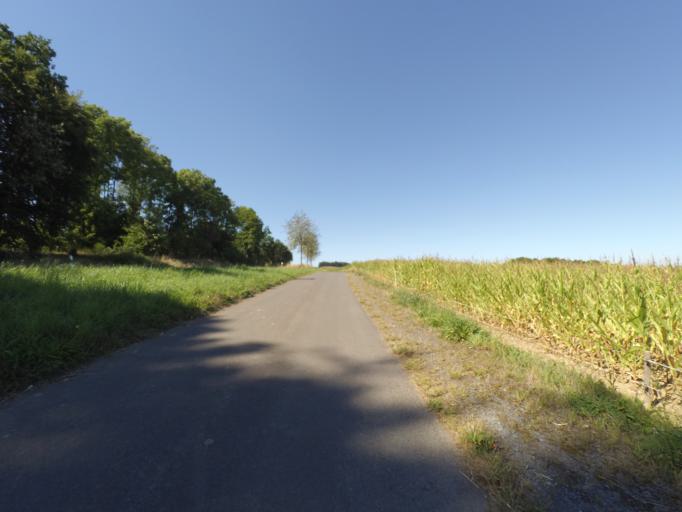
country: DE
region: Rheinland-Pfalz
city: Lutzerath
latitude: 50.1060
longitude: 7.0152
